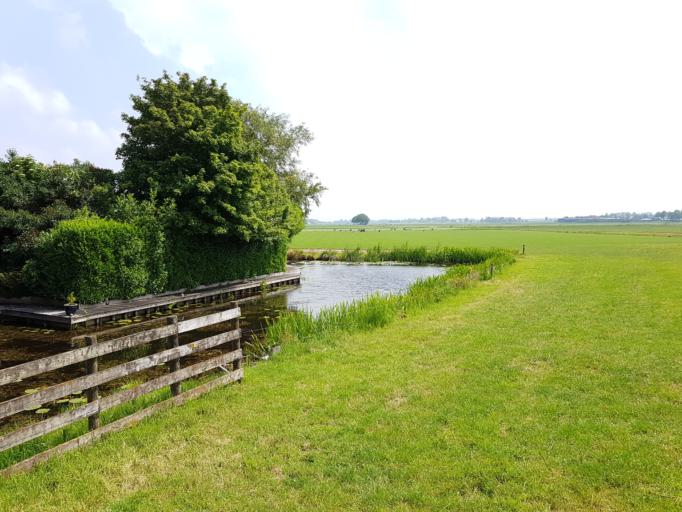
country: NL
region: Friesland
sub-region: Gemeente Boarnsterhim
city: Aldeboarn
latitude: 53.0692
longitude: 5.9517
